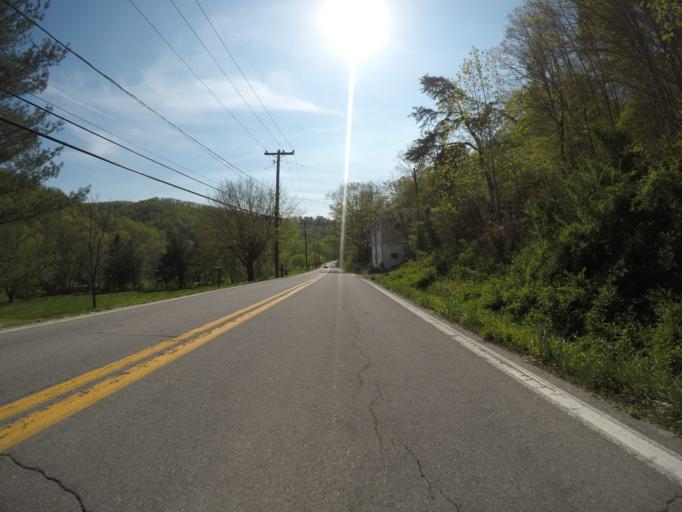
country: US
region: West Virginia
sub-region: Kanawha County
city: Elkview
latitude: 38.4612
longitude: -81.4135
